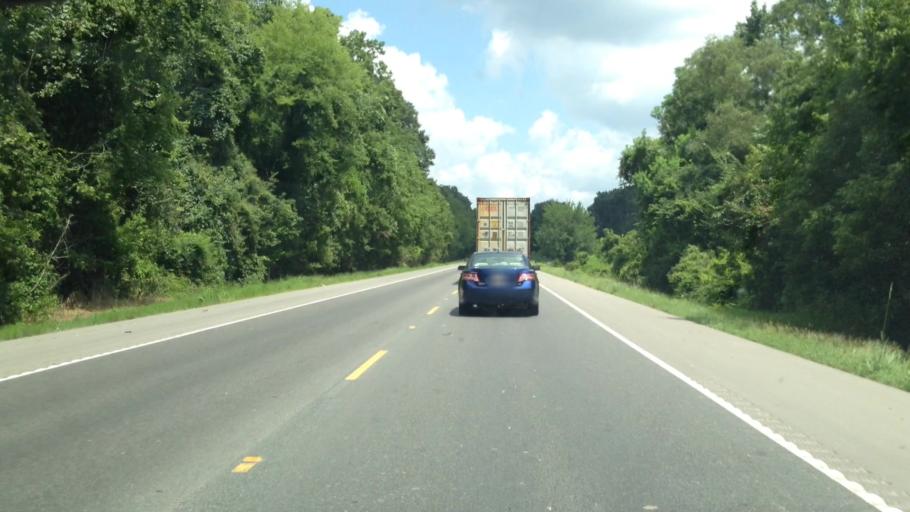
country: US
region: Louisiana
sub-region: Ascension Parish
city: Sorrento
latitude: 30.1581
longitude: -90.8772
